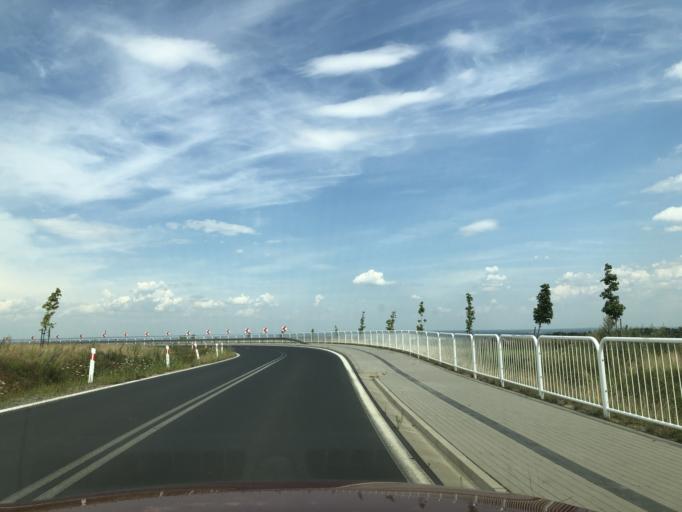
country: PL
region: Lower Silesian Voivodeship
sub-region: Powiat trzebnicki
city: Trzebnica
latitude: 51.3173
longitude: 17.0381
